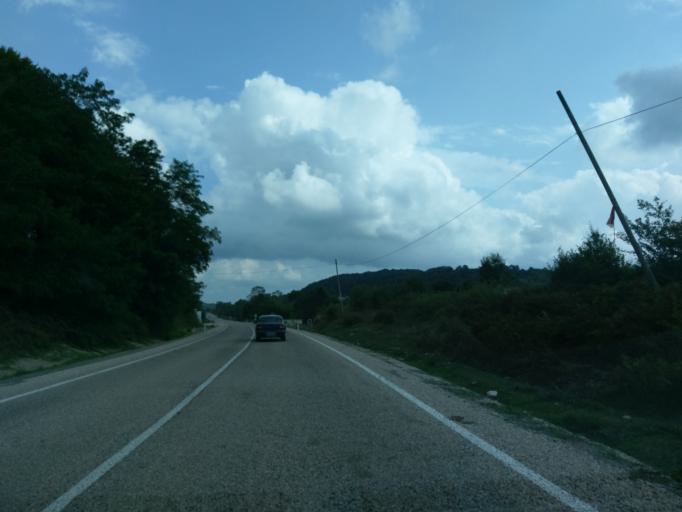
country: TR
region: Sinop
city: Erfelek
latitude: 42.0197
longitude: 34.9831
